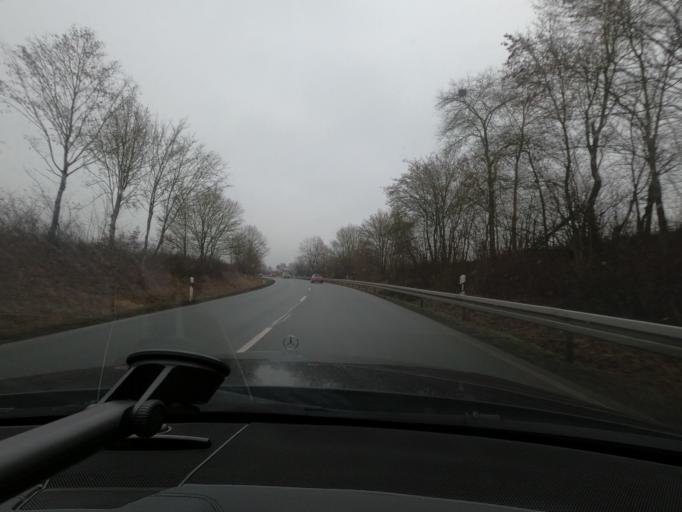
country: DE
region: Hesse
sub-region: Regierungsbezirk Kassel
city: Wolfhagen
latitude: 51.3304
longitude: 9.1527
